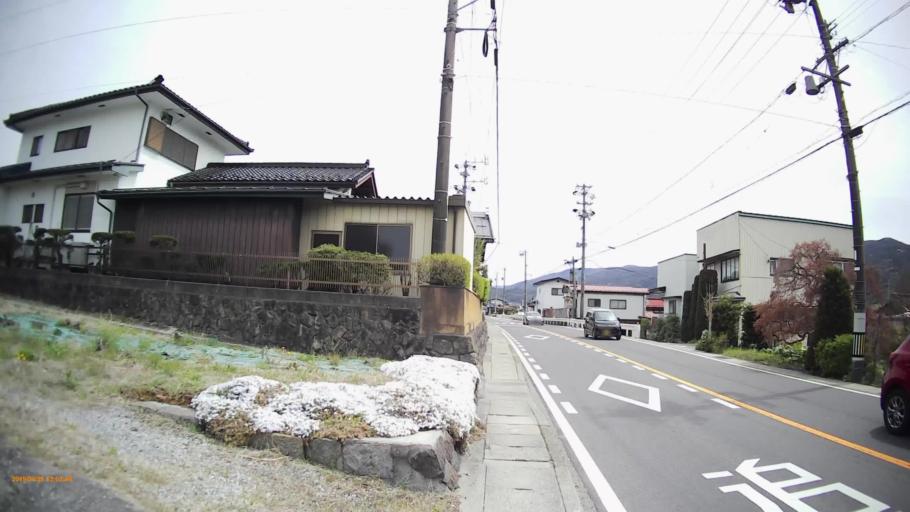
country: JP
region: Nagano
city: Chino
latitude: 36.0053
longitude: 138.1420
